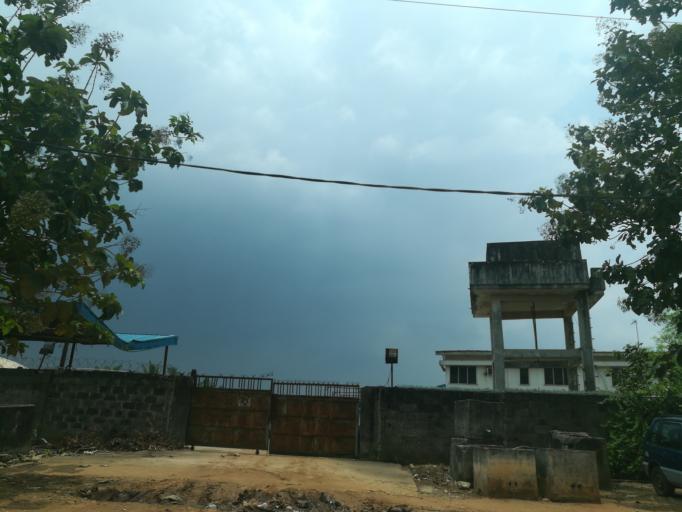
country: NG
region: Lagos
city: Ikorodu
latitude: 6.6135
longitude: 3.5750
